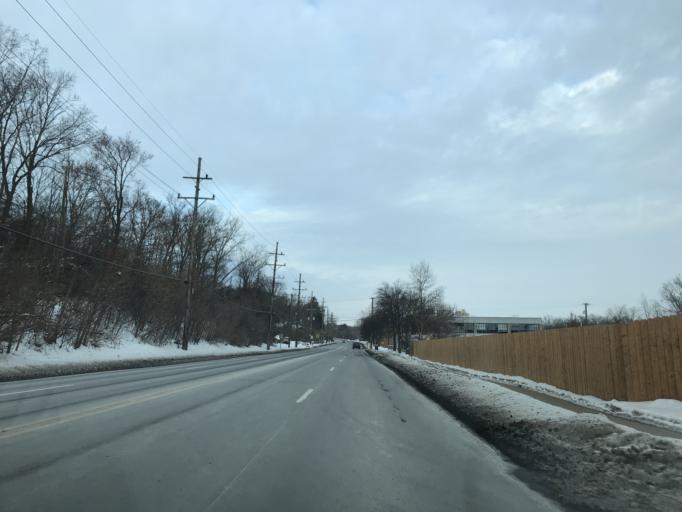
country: US
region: Michigan
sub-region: Washtenaw County
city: Ann Arbor
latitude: 42.2939
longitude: -83.7469
